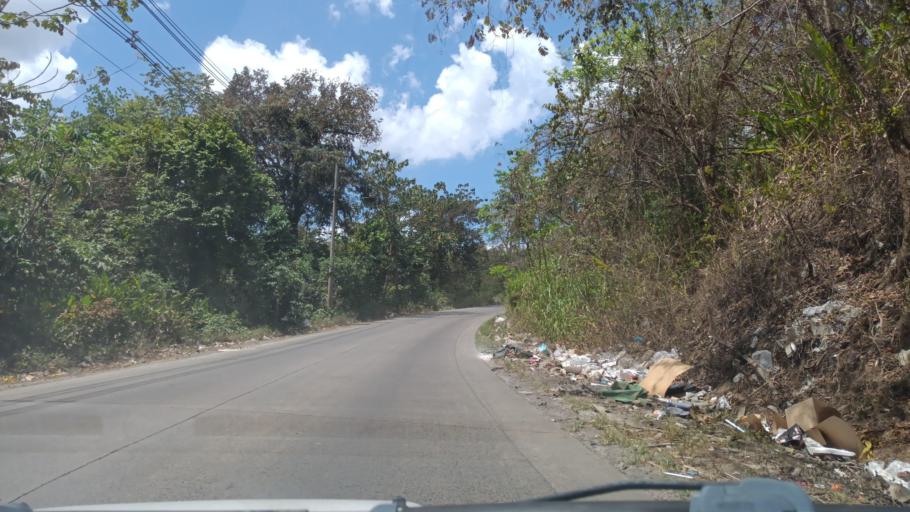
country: PA
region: Panama
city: Las Cumbres
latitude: 9.0422
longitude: -79.5603
